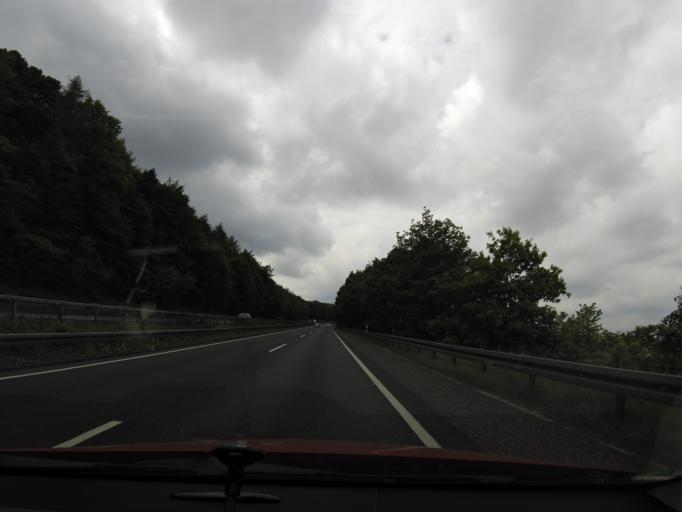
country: DE
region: Hesse
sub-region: Regierungsbezirk Kassel
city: Bad Hersfeld
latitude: 50.8616
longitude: 9.7735
